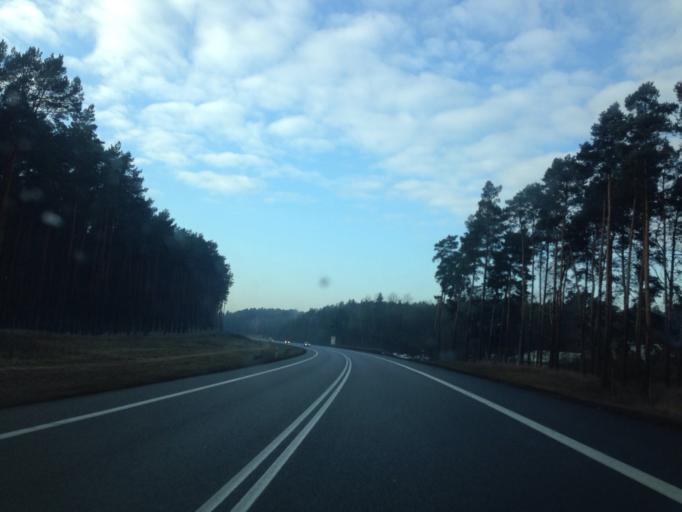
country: PL
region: Kujawsko-Pomorskie
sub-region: Powiat torunski
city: Wielka Nieszawka
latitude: 52.9755
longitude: 18.5302
